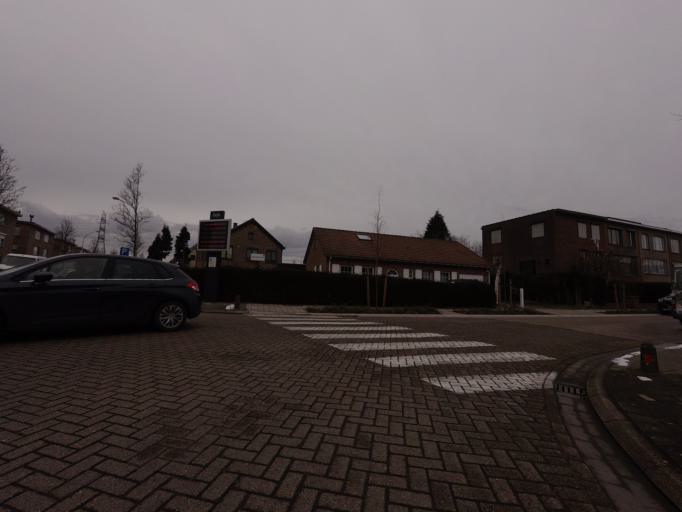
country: BE
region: Flanders
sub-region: Provincie Antwerpen
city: Boom
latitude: 51.1109
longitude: 4.3647
